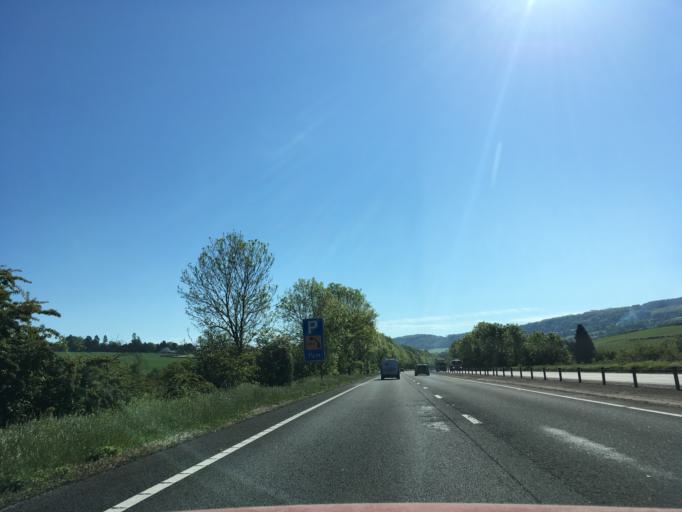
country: GB
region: Wales
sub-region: Monmouthshire
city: Mitchel Troy
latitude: 51.7896
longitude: -2.7596
